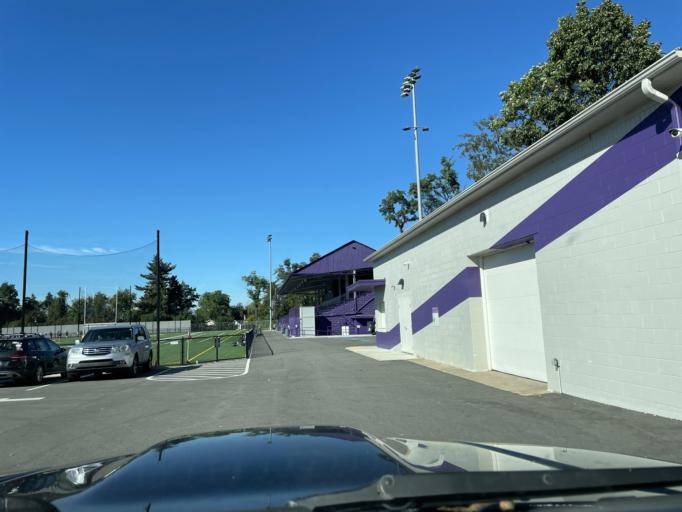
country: US
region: Pennsylvania
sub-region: Allegheny County
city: Wilkinsburg
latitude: 40.4411
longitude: -79.8721
